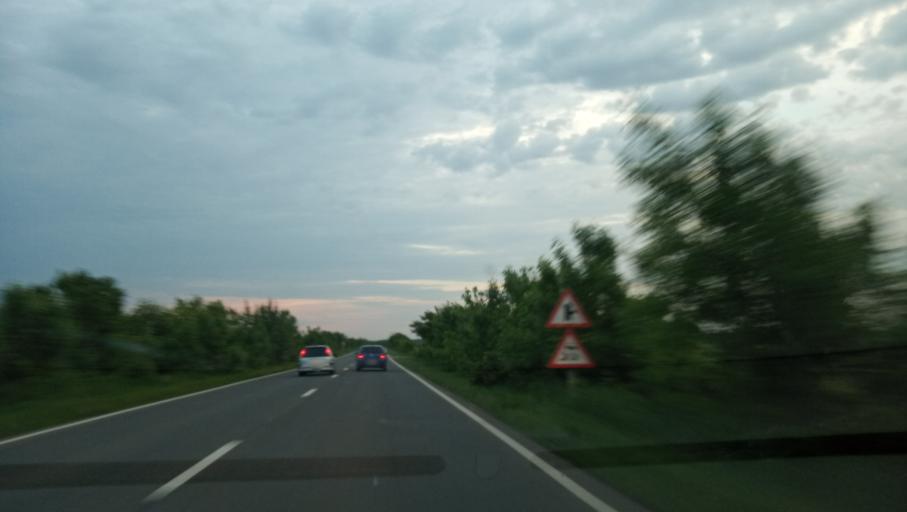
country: RO
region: Timis
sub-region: Comuna Padureni
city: Padureni
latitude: 45.6070
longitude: 21.1963
